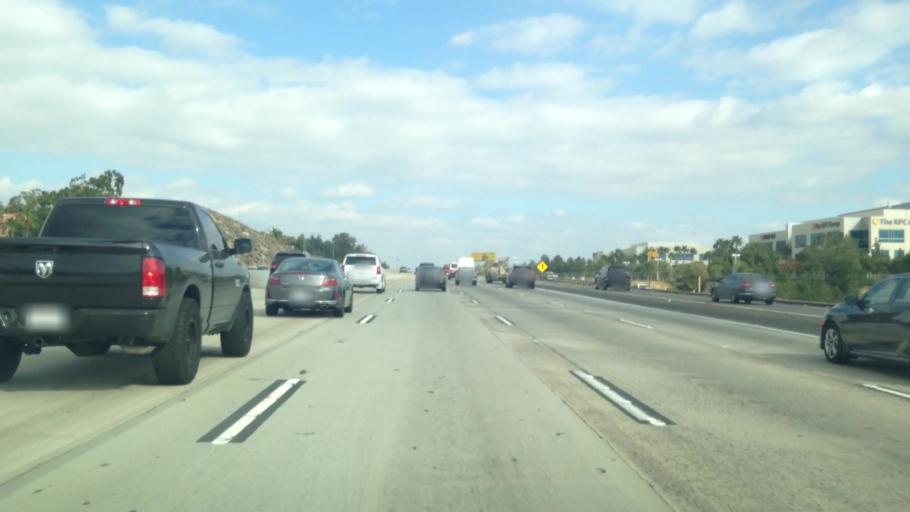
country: US
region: California
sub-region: Riverside County
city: Home Gardens
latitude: 33.8865
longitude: -117.5172
